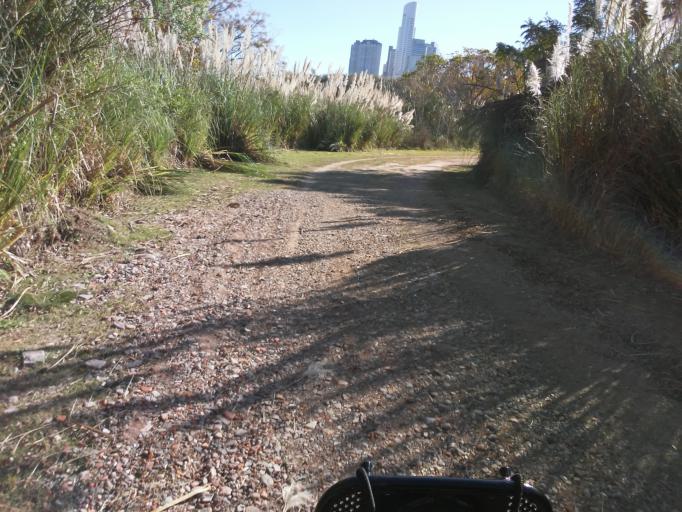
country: AR
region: Buenos Aires F.D.
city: Buenos Aires
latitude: -34.6166
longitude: -58.3485
